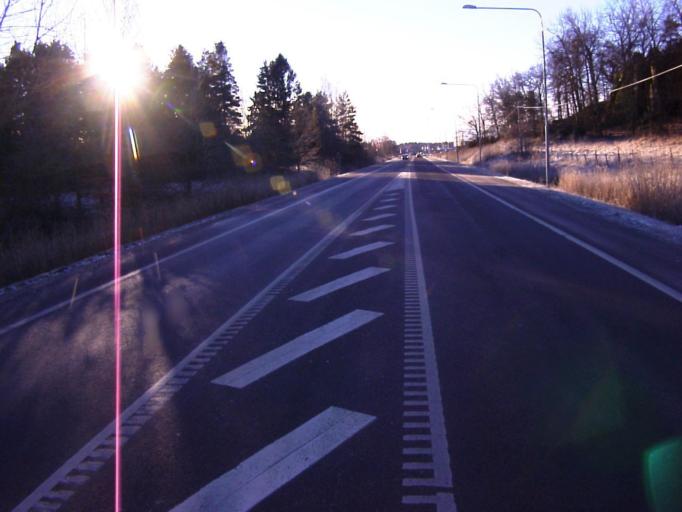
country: SE
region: Soedermanland
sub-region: Eskilstuna Kommun
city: Torshalla
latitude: 59.3998
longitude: 16.4721
